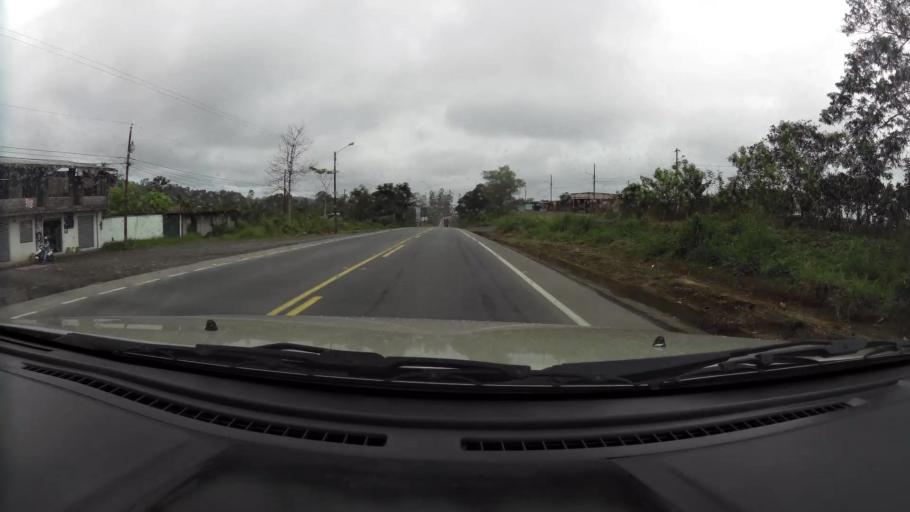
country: EC
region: Santo Domingo de los Tsachilas
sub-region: Canton Santo Domingo de los Colorados
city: Santo Domingo de los Colorados
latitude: -0.2665
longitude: -79.1414
